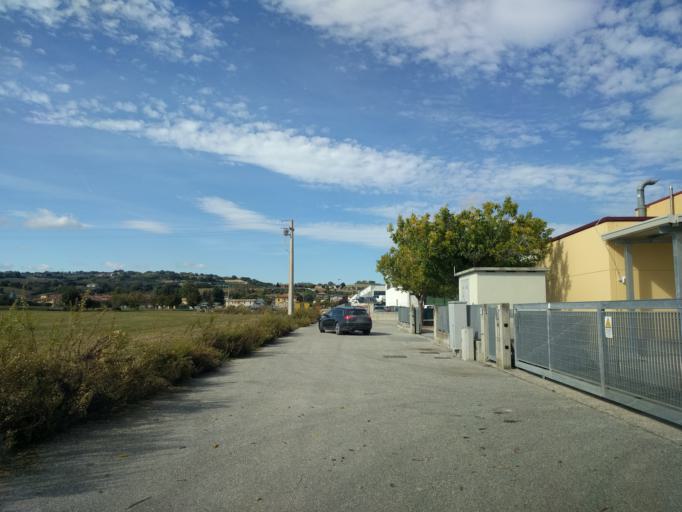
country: IT
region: The Marches
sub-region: Provincia di Pesaro e Urbino
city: Lucrezia
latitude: 43.7605
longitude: 12.9348
